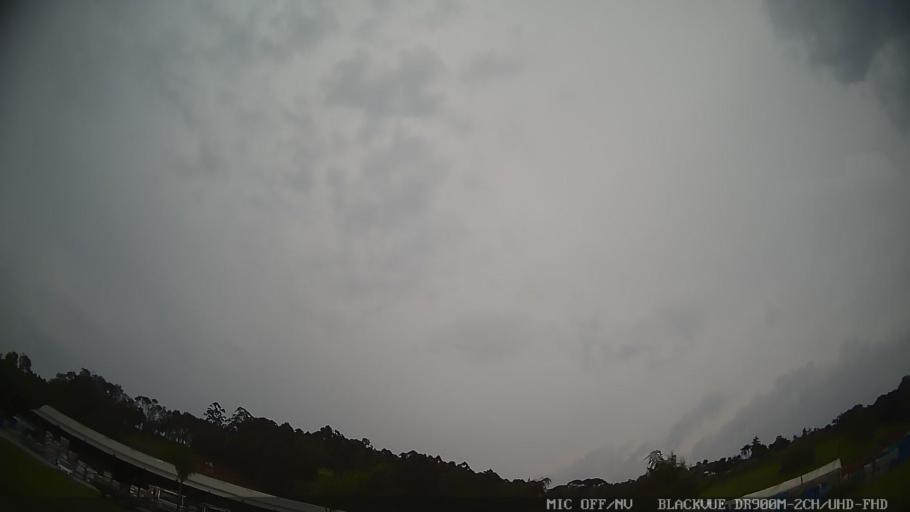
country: BR
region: Sao Paulo
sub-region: Braganca Paulista
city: Braganca Paulista
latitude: -22.9679
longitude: -46.5540
